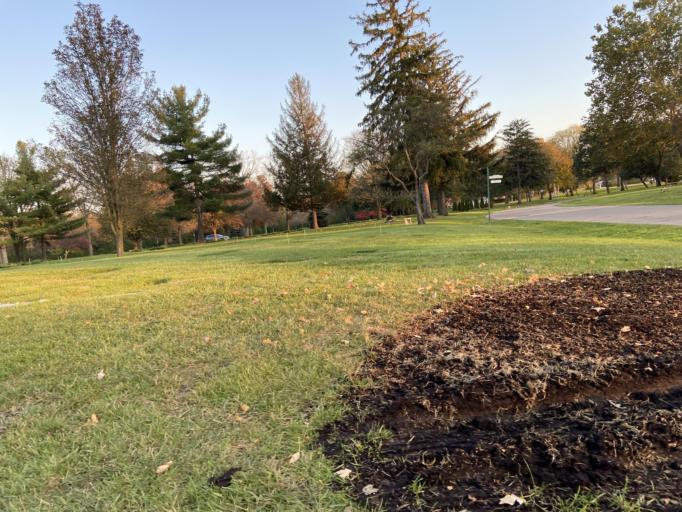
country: US
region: Michigan
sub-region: Wayne County
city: Redford
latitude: 42.4161
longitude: -83.3278
